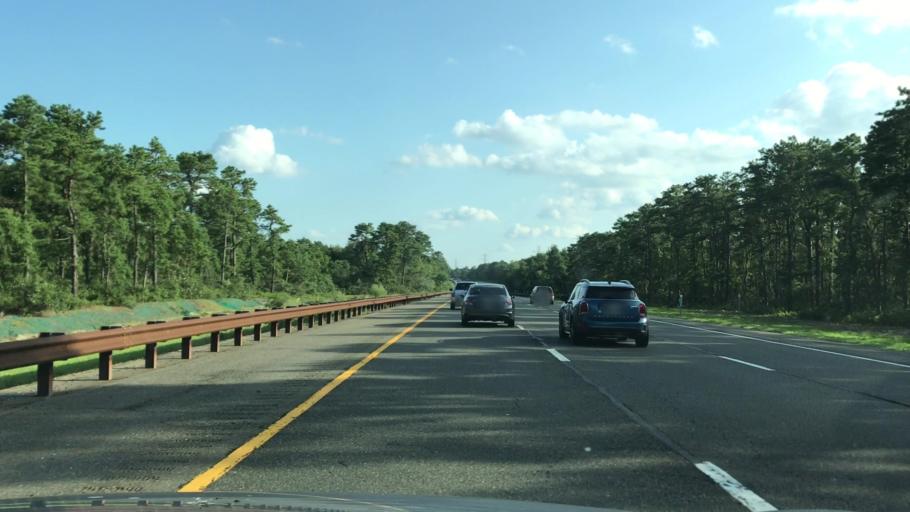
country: US
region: New Jersey
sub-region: Ocean County
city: Forked River
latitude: 39.8328
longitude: -74.2261
